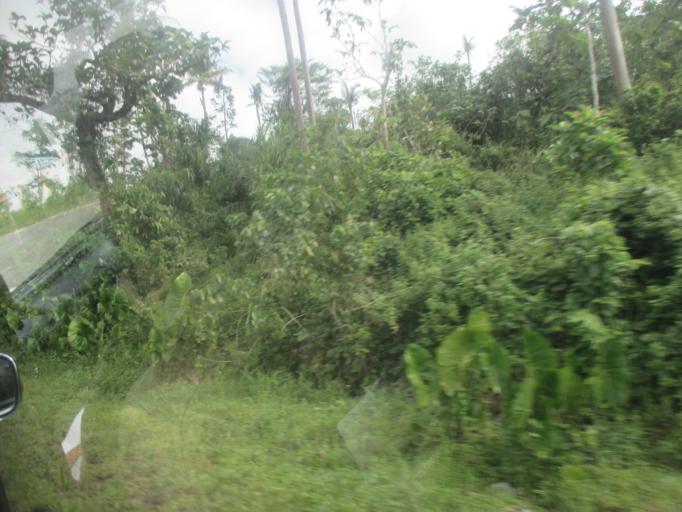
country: PH
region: Eastern Visayas
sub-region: Province of Eastern Samar
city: Lawa-an
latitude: 11.1290
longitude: 125.3222
